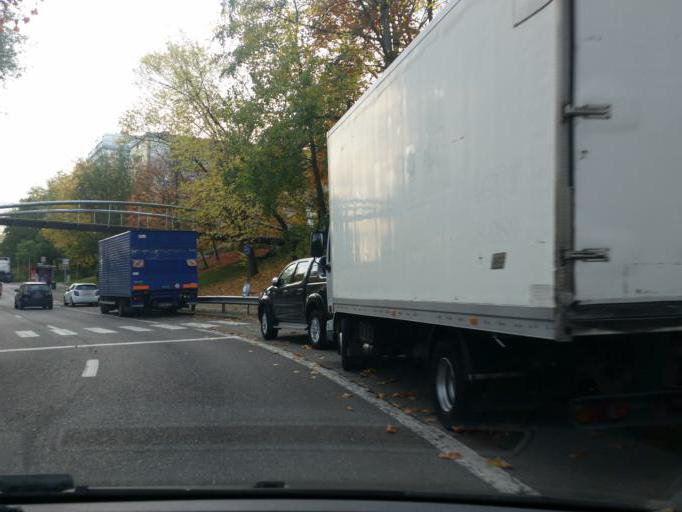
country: BE
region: Flanders
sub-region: Provincie Vlaams-Brabant
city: Dilbeek
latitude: 50.8444
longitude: 4.2958
